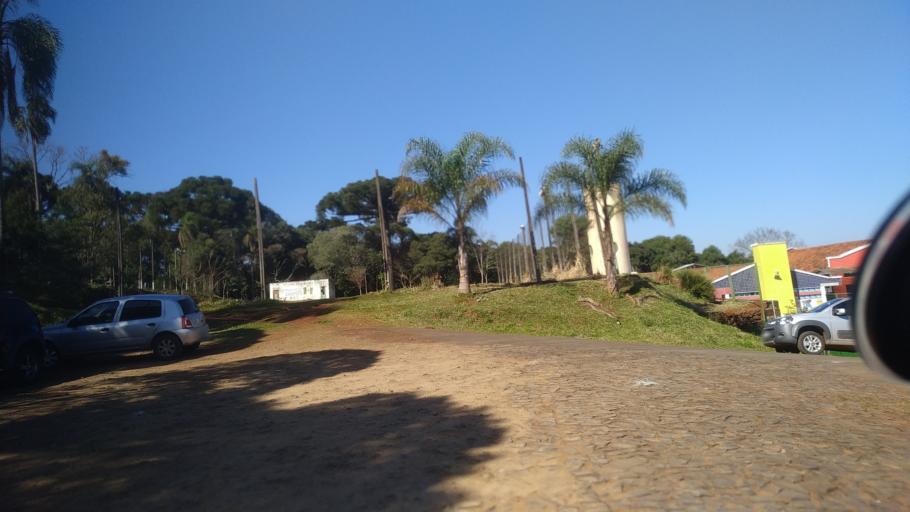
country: BR
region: Santa Catarina
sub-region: Chapeco
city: Chapeco
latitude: -27.0903
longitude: -52.5887
